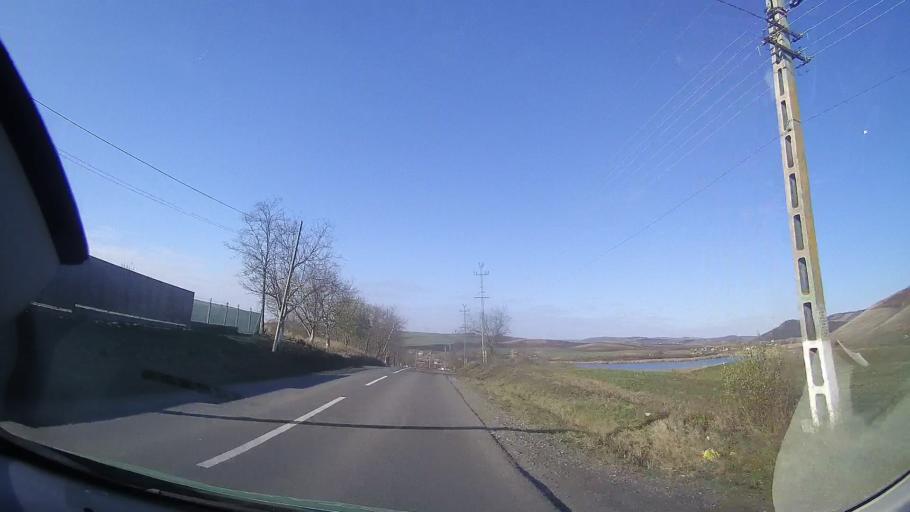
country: RO
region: Mures
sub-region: Comuna Saulia
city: Saulia
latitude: 46.6515
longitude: 24.1827
